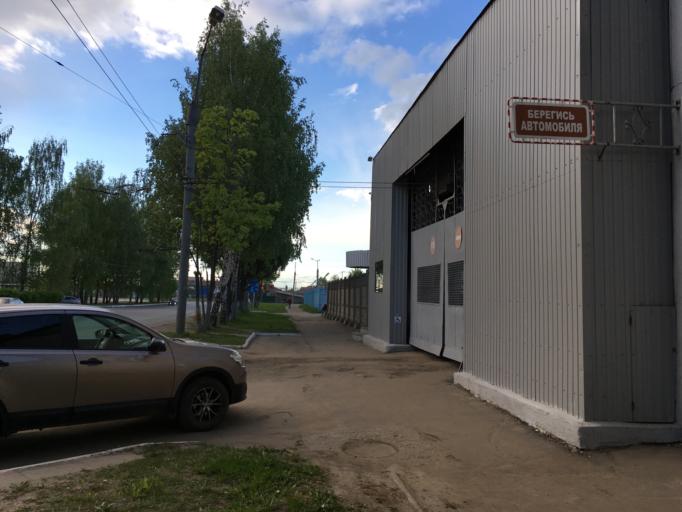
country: RU
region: Mariy-El
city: Yoshkar-Ola
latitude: 56.6527
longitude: 47.8751
